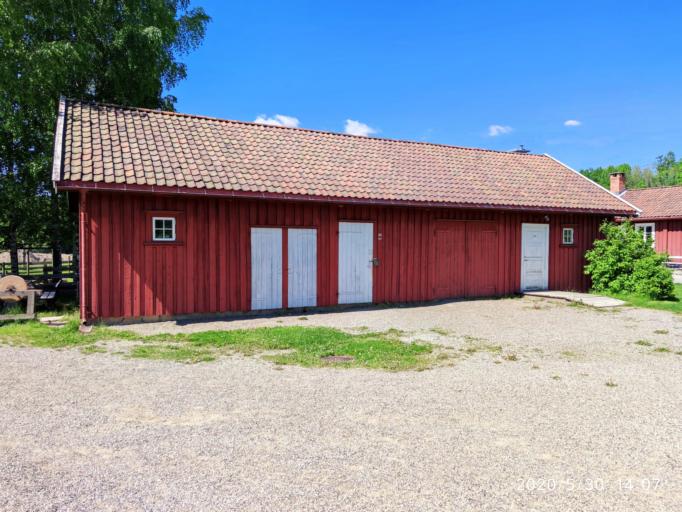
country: NO
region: Buskerud
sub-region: Lier
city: Tranby
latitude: 59.7992
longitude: 10.2579
